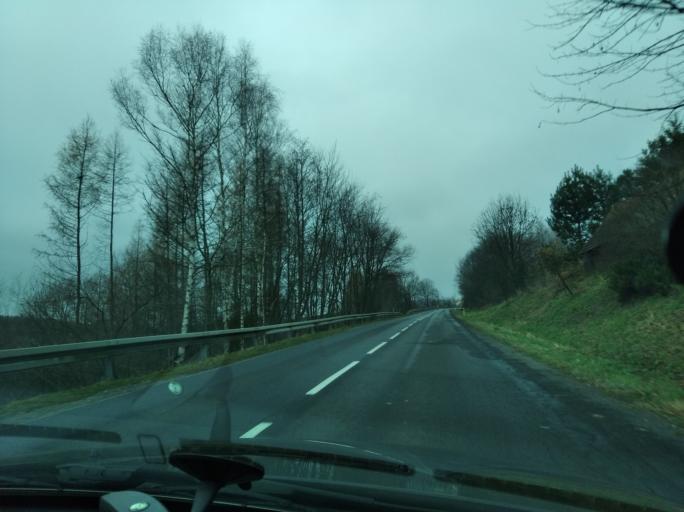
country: PL
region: Subcarpathian Voivodeship
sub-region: Powiat przeworski
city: Jawornik Polski
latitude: 49.8833
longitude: 22.2395
